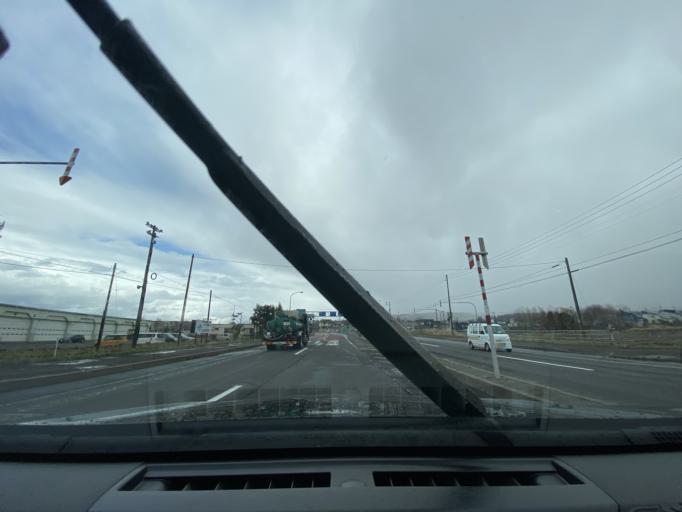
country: JP
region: Hokkaido
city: Fukagawa
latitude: 43.6979
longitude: 142.0692
